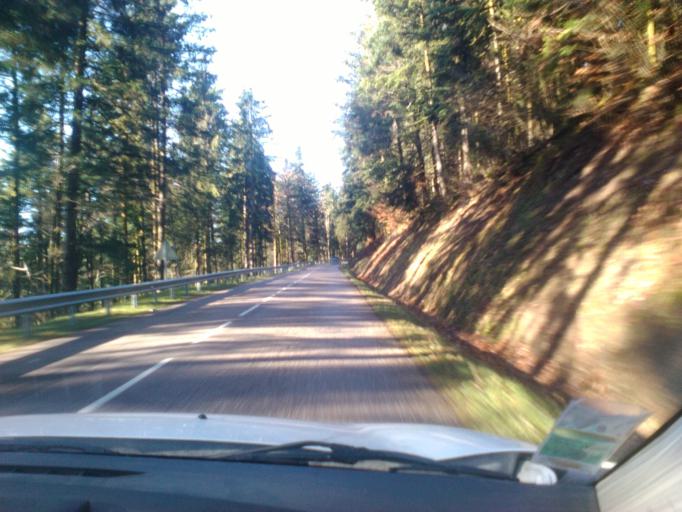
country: FR
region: Lorraine
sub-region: Departement des Vosges
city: Remiremont
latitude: 47.9694
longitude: 6.5337
